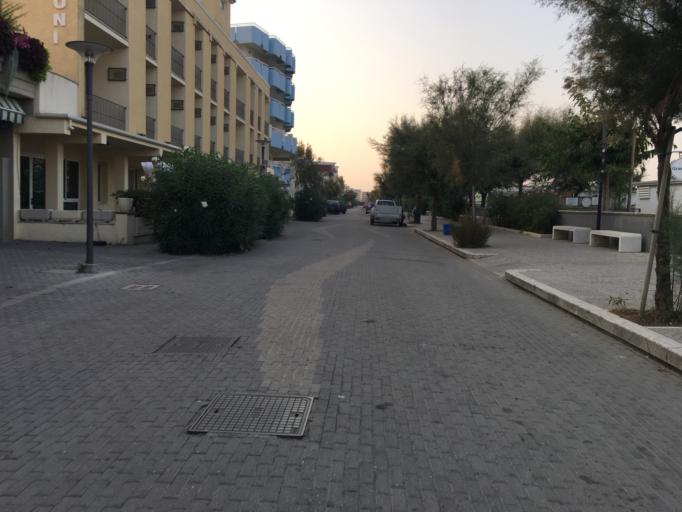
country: IT
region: Emilia-Romagna
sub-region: Forli-Cesena
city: San Mauro a Mare
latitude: 44.1642
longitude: 12.4471
